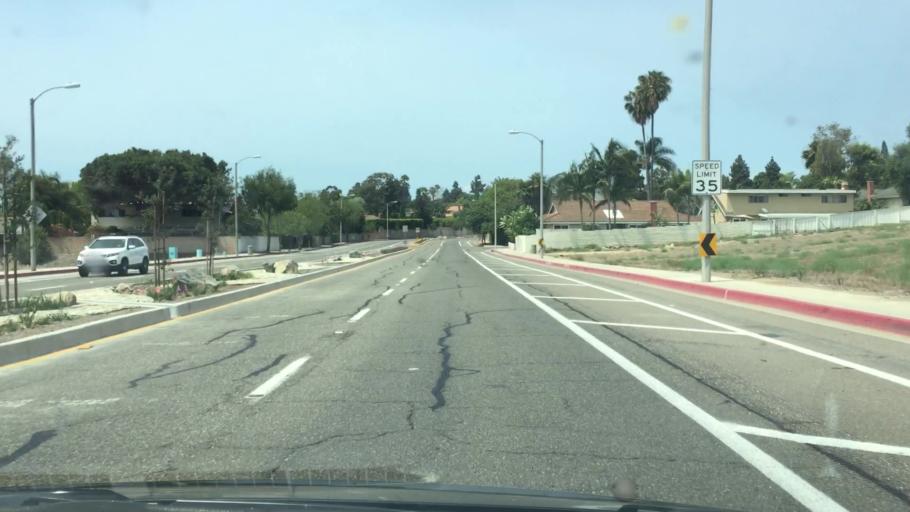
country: US
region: California
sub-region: Orange County
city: Costa Mesa
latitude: 33.6678
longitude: -117.9372
